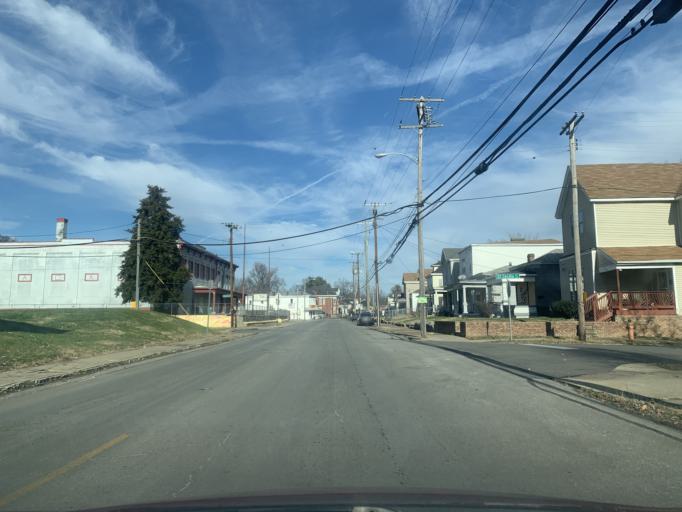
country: US
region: Kentucky
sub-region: Jefferson County
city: Louisville
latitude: 38.2644
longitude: -85.7931
